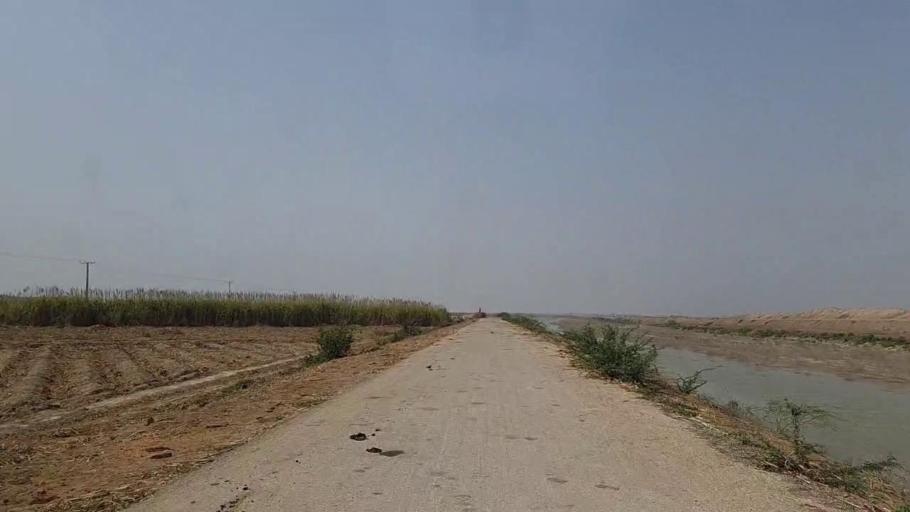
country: PK
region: Sindh
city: Naukot
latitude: 24.7974
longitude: 69.3406
